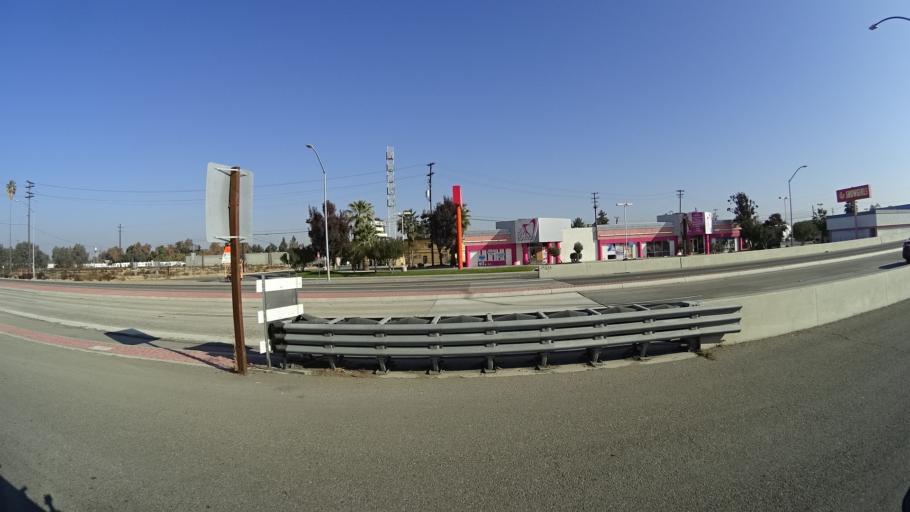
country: US
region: California
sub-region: Kern County
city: Bakersfield
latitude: 35.3879
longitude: -119.0209
